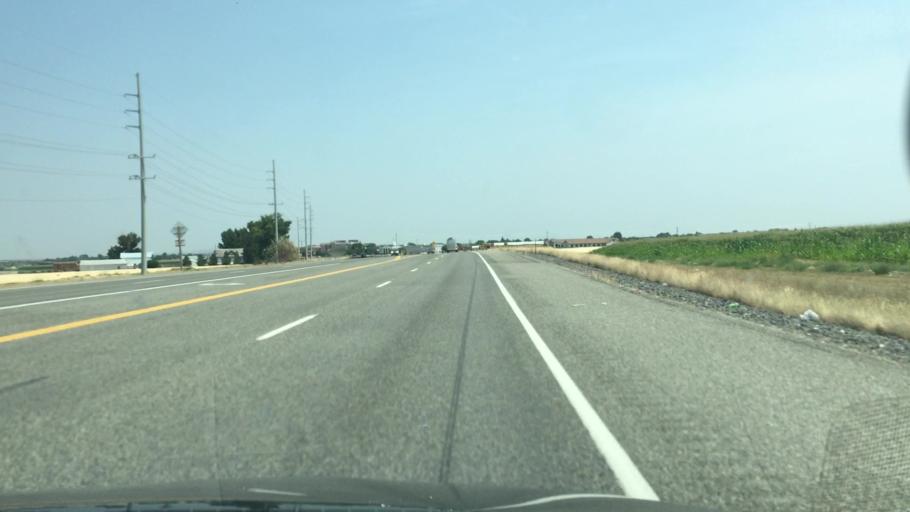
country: US
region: Idaho
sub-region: Twin Falls County
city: Twin Falls
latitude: 42.5925
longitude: -114.5150
